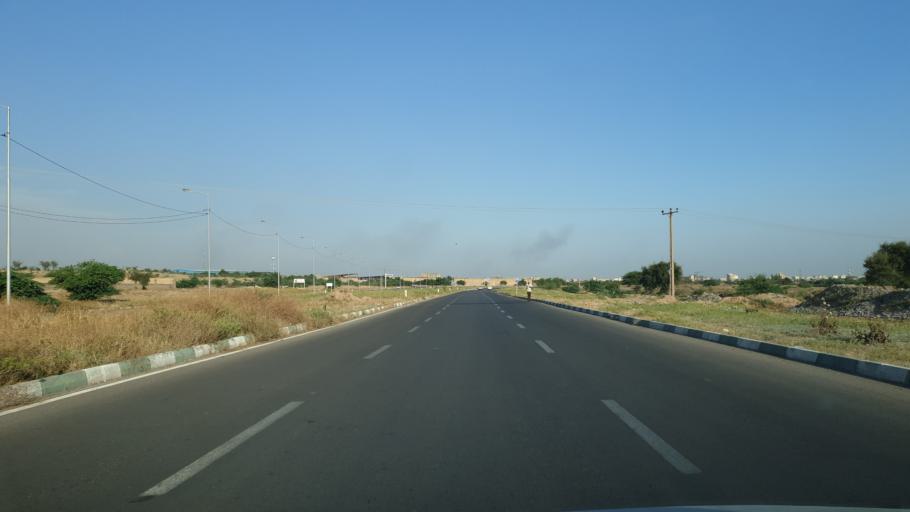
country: IR
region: Khuzestan
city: Dezful
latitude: 32.3896
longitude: 48.3709
